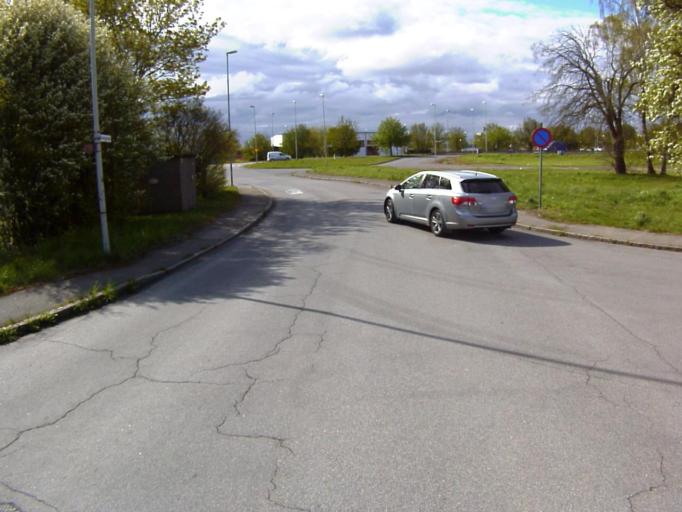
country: SE
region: Skane
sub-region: Kristianstads Kommun
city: Kristianstad
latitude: 56.0232
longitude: 14.1493
